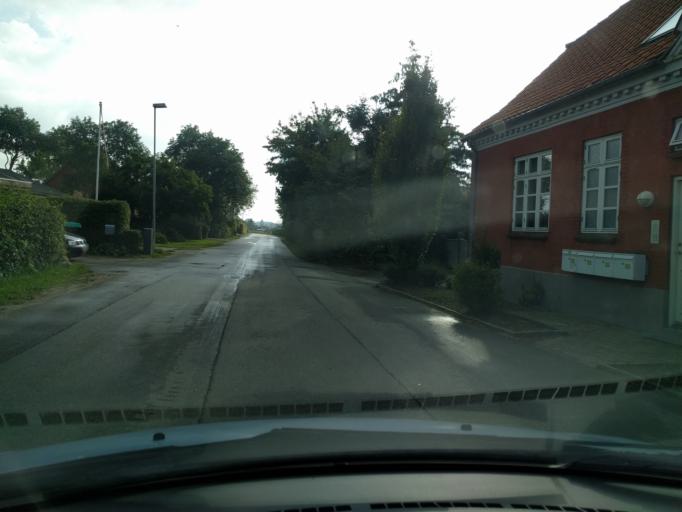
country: DK
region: South Denmark
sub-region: Kerteminde Kommune
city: Munkebo
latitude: 55.4320
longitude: 10.5856
